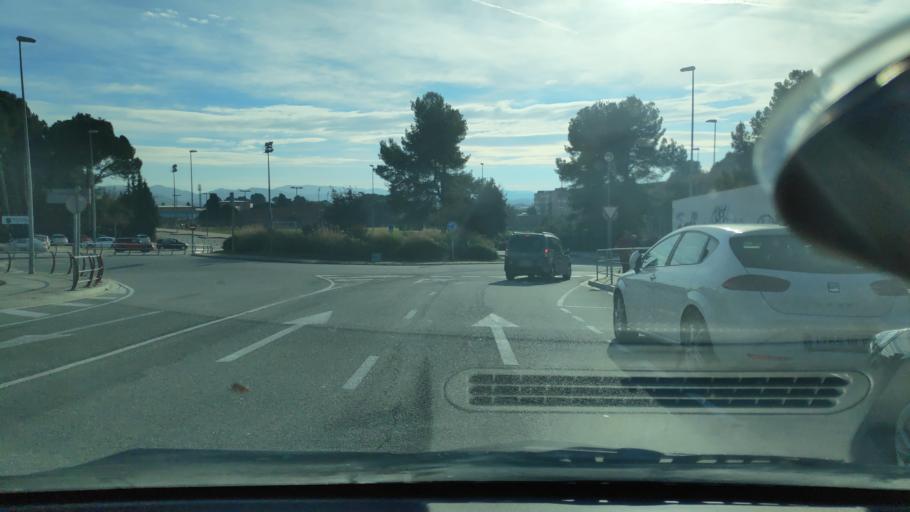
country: ES
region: Catalonia
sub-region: Provincia de Barcelona
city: Sant Cugat del Valles
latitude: 41.4872
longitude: 2.0772
